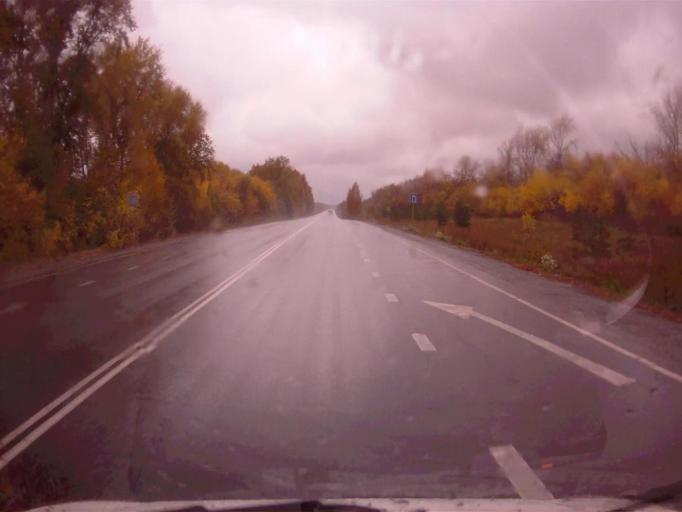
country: RU
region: Chelyabinsk
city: Argayash
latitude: 55.4347
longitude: 60.9794
